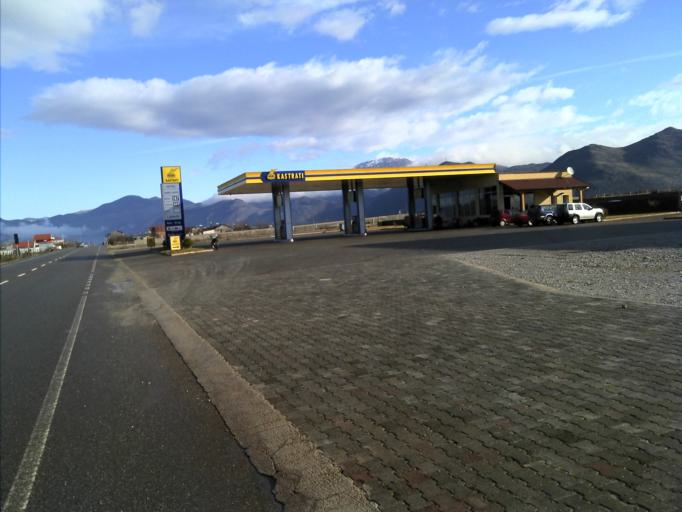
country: AL
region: Shkoder
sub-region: Rrethi i Malesia e Madhe
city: Koplik
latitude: 42.2527
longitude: 19.4267
